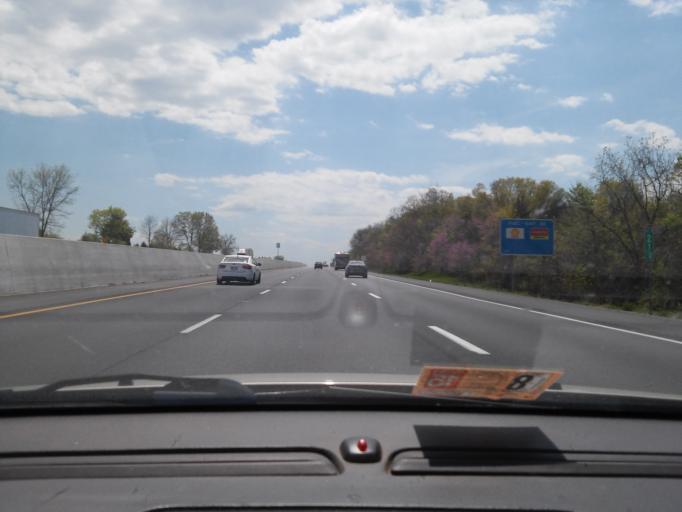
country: US
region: Maryland
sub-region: Washington County
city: Williamsport
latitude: 39.5543
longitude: -77.9068
